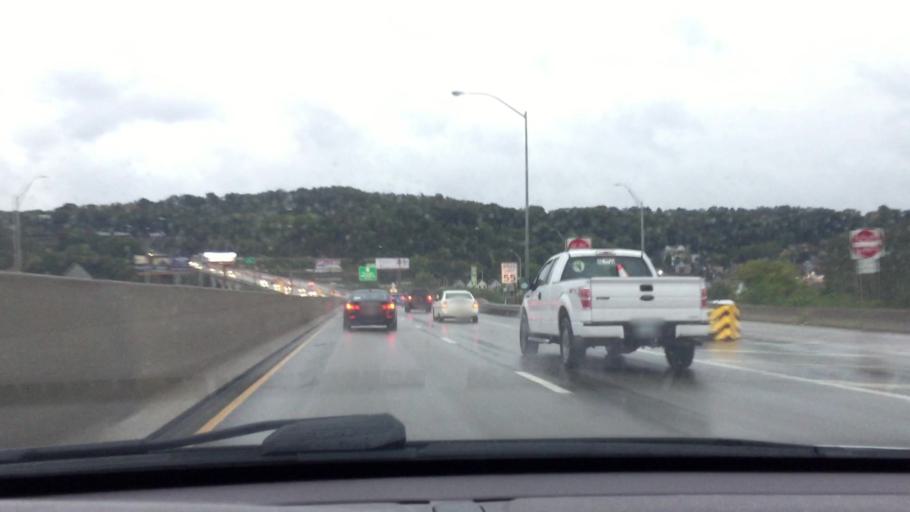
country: US
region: Pennsylvania
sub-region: Allegheny County
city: Carnegie
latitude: 40.4157
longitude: -80.0846
